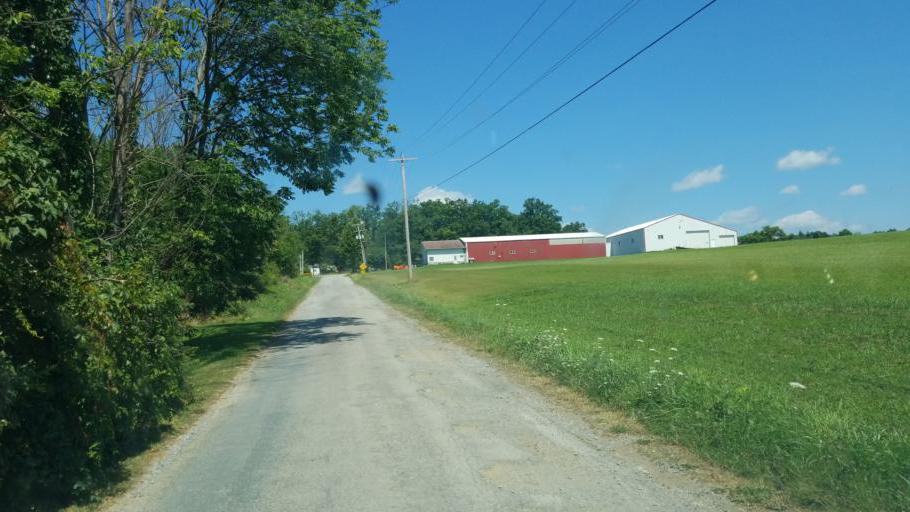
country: US
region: Pennsylvania
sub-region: Clarion County
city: Knox
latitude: 41.1948
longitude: -79.5272
